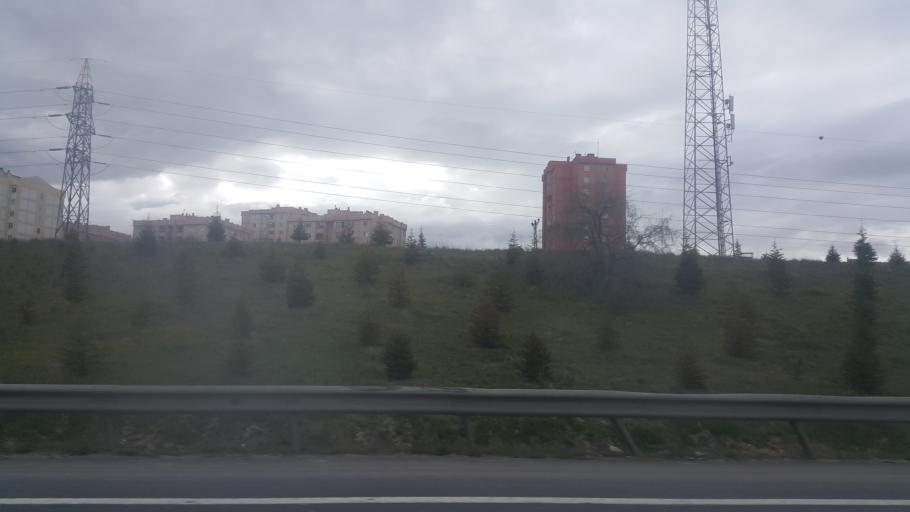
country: TR
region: Ankara
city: Etimesgut
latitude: 39.9725
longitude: 32.6335
